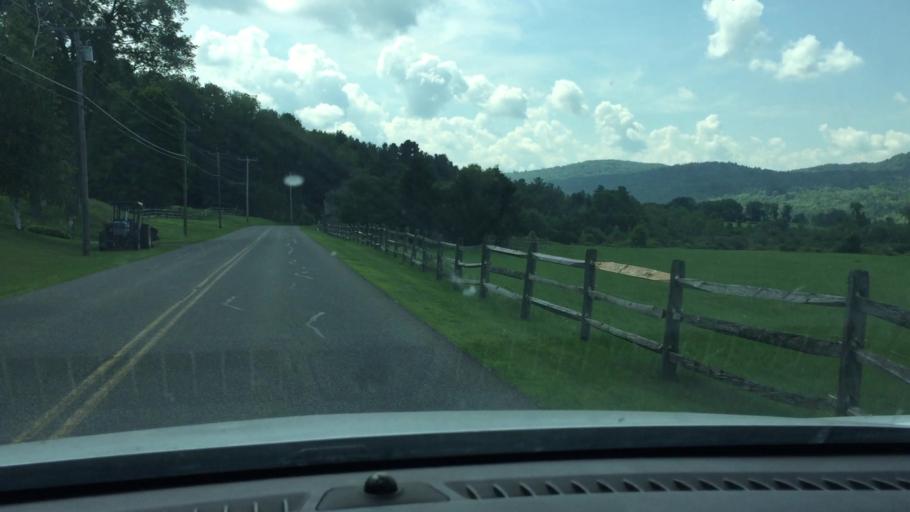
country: US
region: Massachusetts
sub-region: Berkshire County
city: Lee
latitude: 42.2396
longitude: -73.1960
